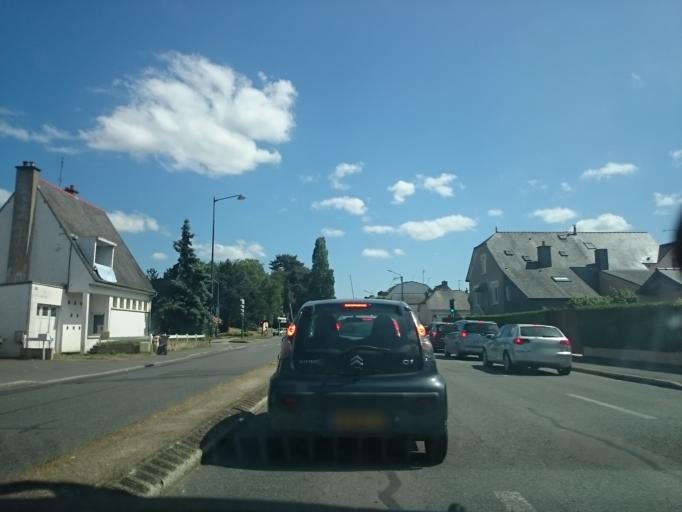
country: FR
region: Brittany
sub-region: Departement d'Ille-et-Vilaine
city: Rennes
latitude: 48.1285
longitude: -1.6837
